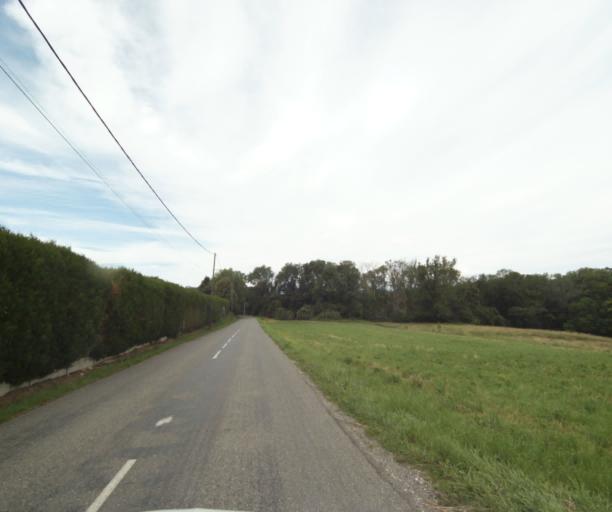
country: FR
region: Rhone-Alpes
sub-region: Departement de la Haute-Savoie
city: Allinges
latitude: 46.3499
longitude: 6.4508
